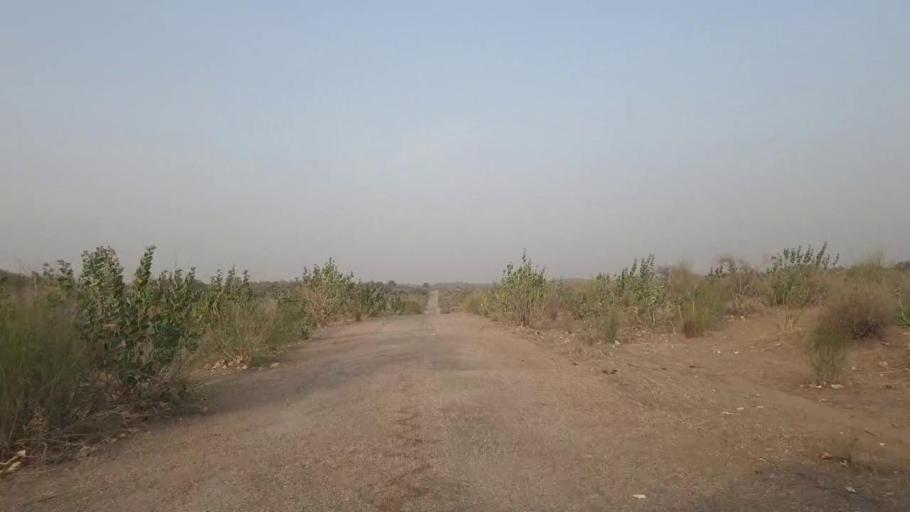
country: PK
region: Sindh
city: Chor
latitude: 25.5086
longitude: 69.9396
